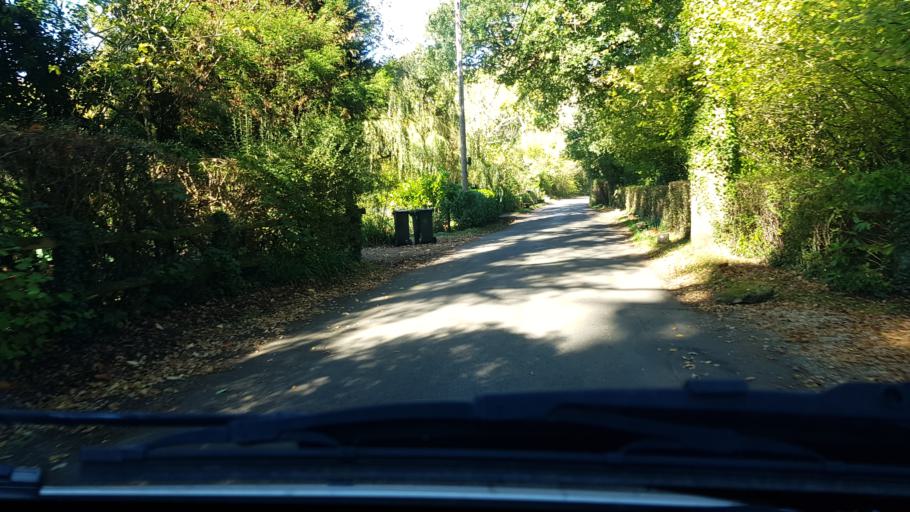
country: GB
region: England
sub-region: Surrey
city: Ockley
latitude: 51.1468
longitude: -0.3378
